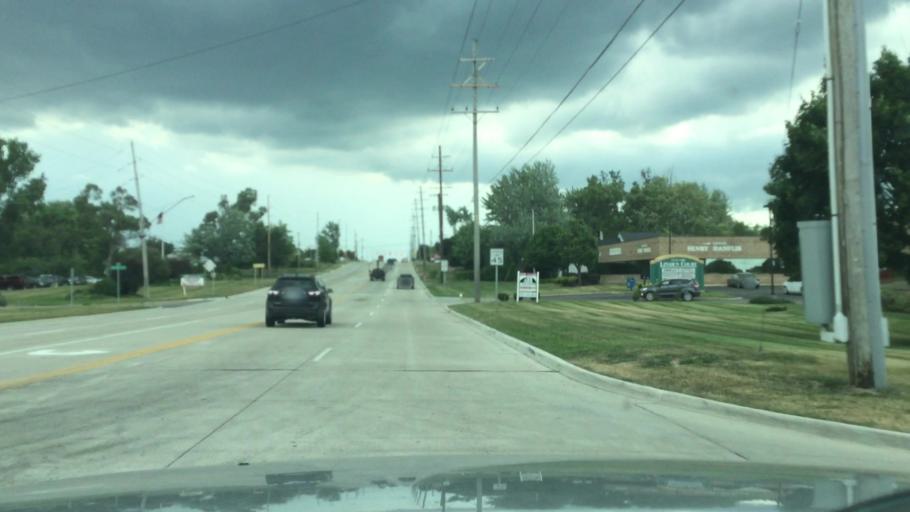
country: US
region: Michigan
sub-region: Genesee County
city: Swartz Creek
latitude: 43.0067
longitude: -83.7729
